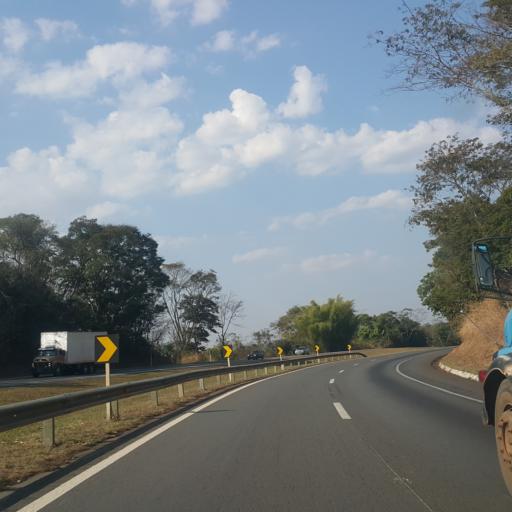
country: BR
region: Goias
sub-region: Abadiania
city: Abadiania
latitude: -16.1638
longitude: -48.6320
